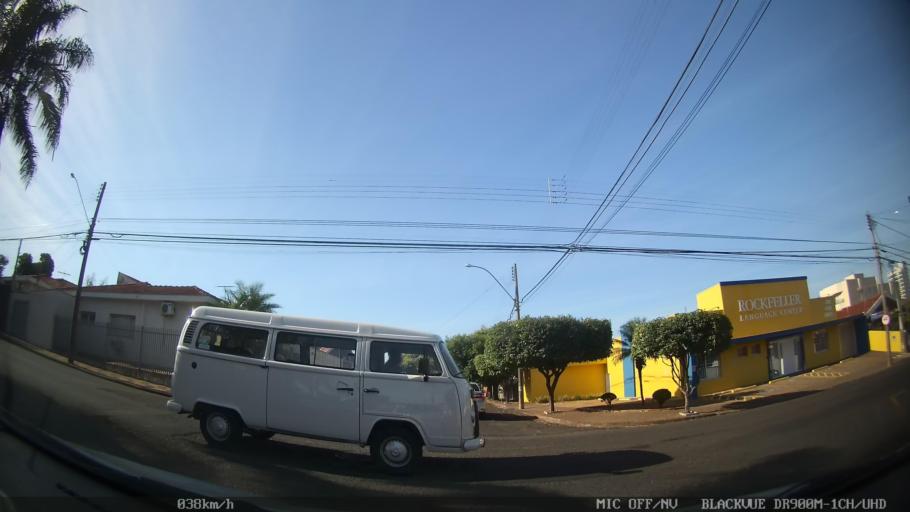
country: BR
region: Sao Paulo
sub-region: Sao Jose Do Rio Preto
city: Sao Jose do Rio Preto
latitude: -20.8075
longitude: -49.3901
